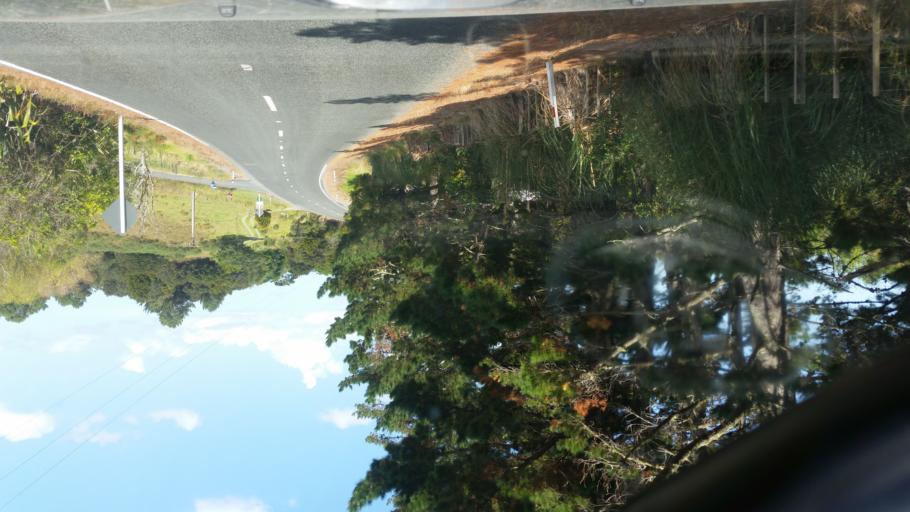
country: NZ
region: Northland
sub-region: Whangarei
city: Ruakaka
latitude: -36.1404
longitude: 174.2246
